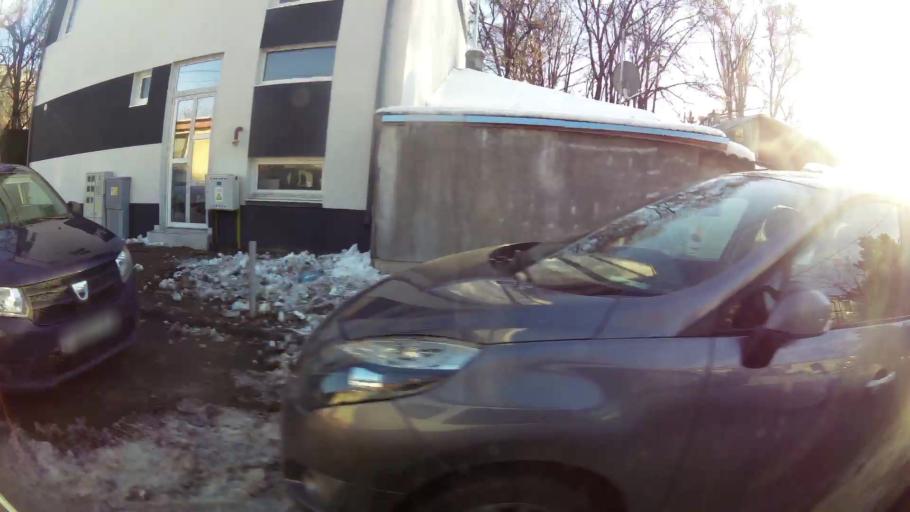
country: RO
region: Bucuresti
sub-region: Municipiul Bucuresti
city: Bucuresti
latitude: 44.3963
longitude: 26.0930
